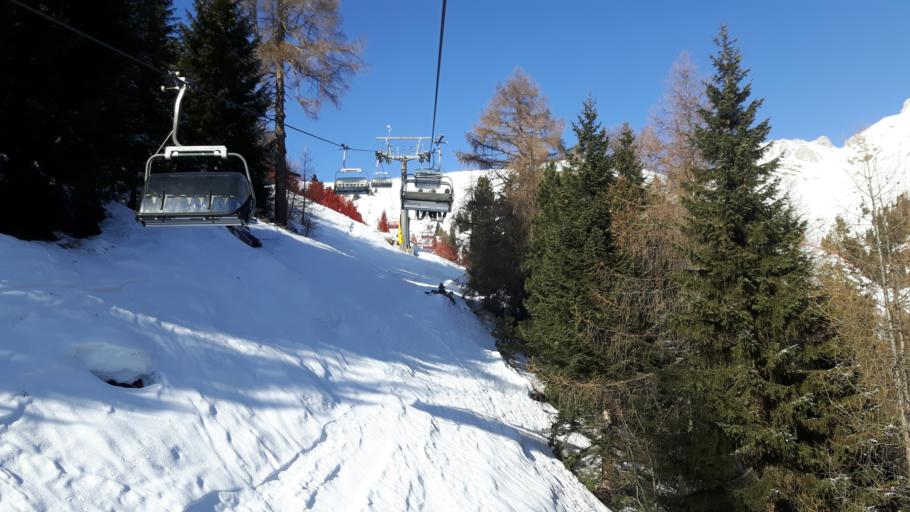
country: IT
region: Trentino-Alto Adige
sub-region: Provincia di Trento
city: Predazzo
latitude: 46.3423
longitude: 11.5704
